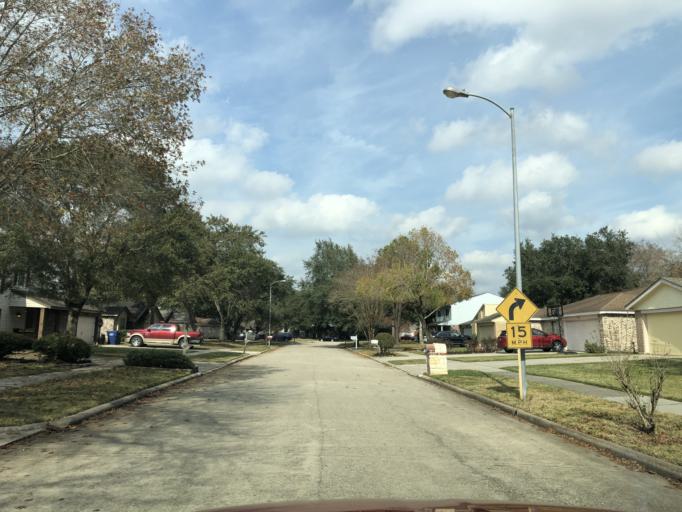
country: US
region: Texas
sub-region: Harris County
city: Tomball
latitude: 30.0381
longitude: -95.5442
